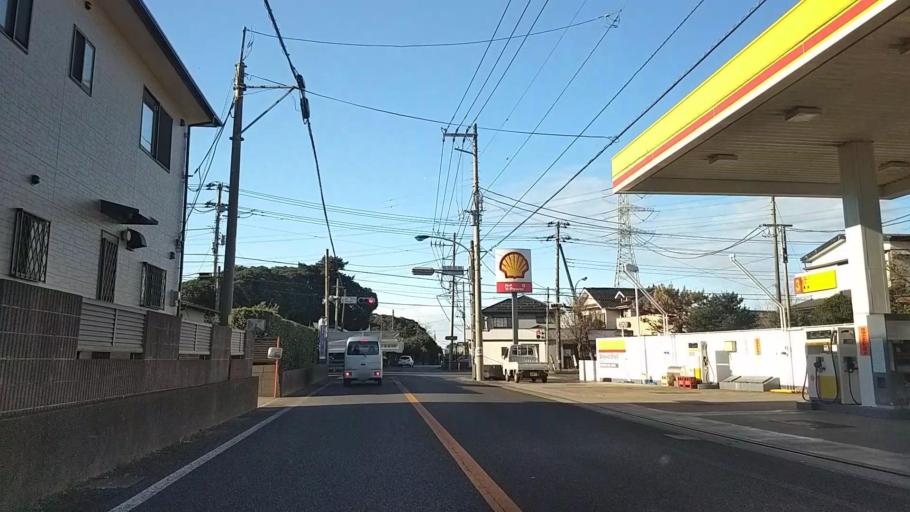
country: JP
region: Chiba
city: Futtsu
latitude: 35.3191
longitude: 139.8369
